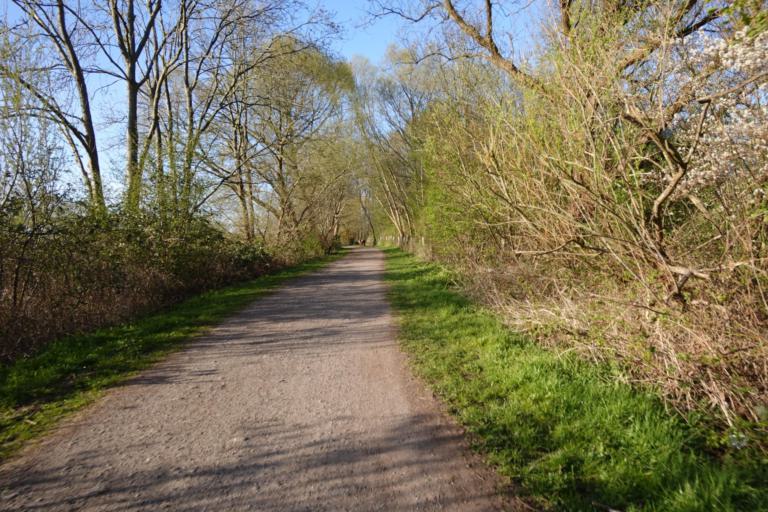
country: DE
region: Schleswig-Holstein
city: Wedel
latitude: 53.5764
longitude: 9.6919
